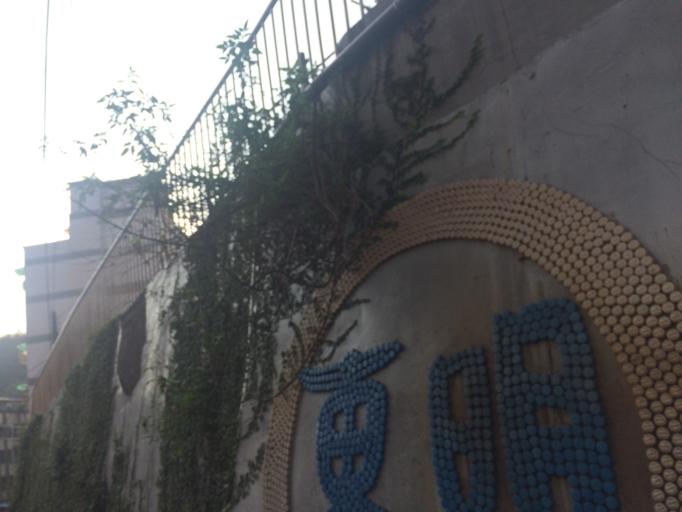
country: TW
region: Taiwan
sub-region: Keelung
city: Keelung
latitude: 25.1278
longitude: 121.7668
